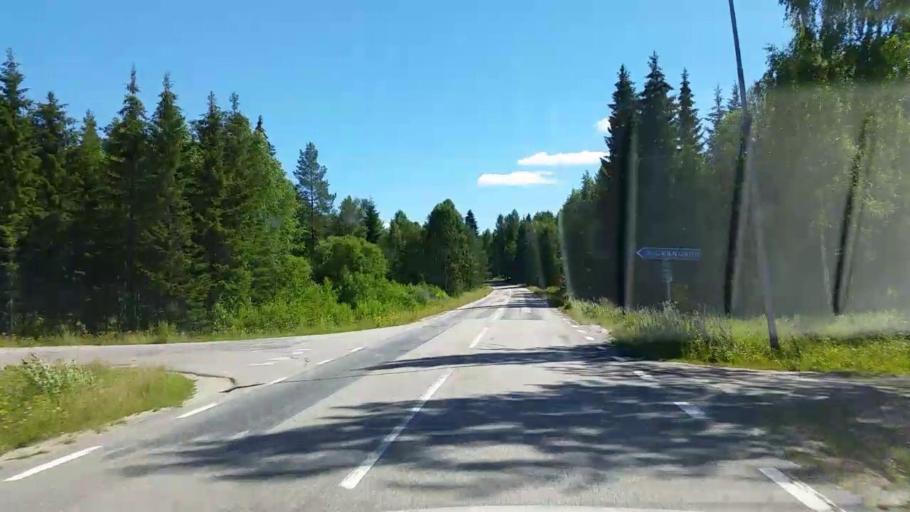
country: SE
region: Gaevleborg
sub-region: Ovanakers Kommun
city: Edsbyn
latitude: 61.3333
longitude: 15.8312
